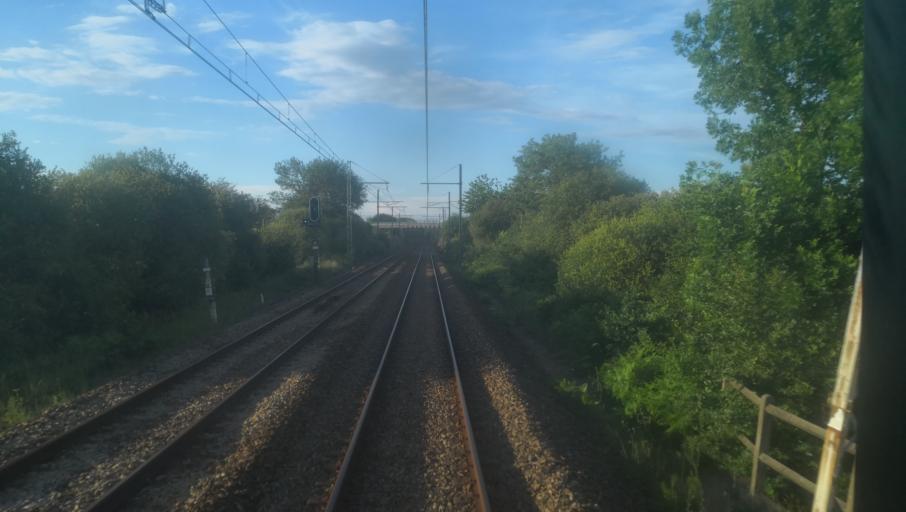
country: FR
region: Centre
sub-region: Departement de l'Indre
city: Luant
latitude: 46.7157
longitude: 1.5775
